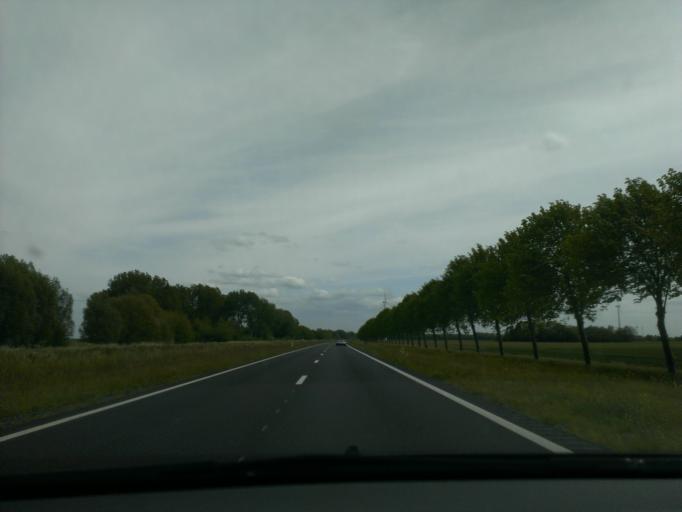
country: NL
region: Gelderland
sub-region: Gemeente Harderwijk
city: Harderwijk
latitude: 52.4278
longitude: 5.5724
